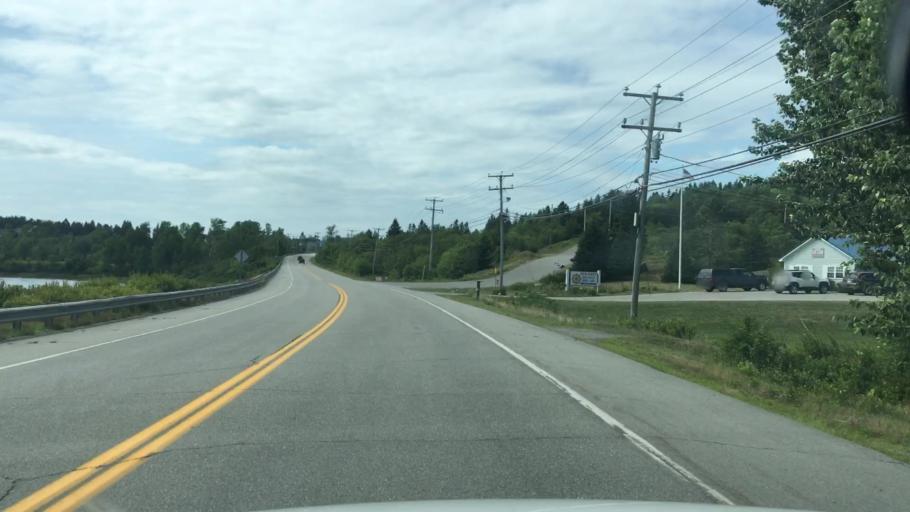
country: US
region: Maine
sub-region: Washington County
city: Eastport
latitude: 44.9251
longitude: -67.0171
